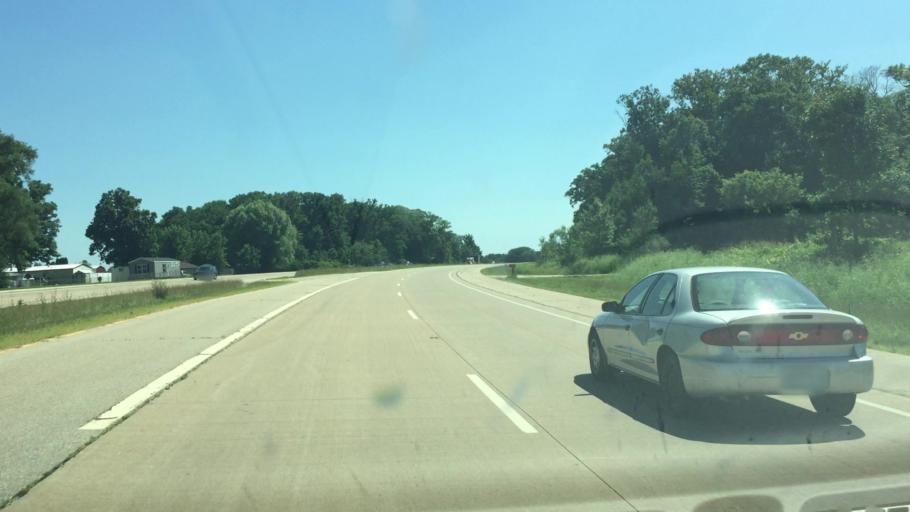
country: US
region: Wisconsin
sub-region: Grant County
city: Platteville
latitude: 42.6935
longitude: -90.5292
